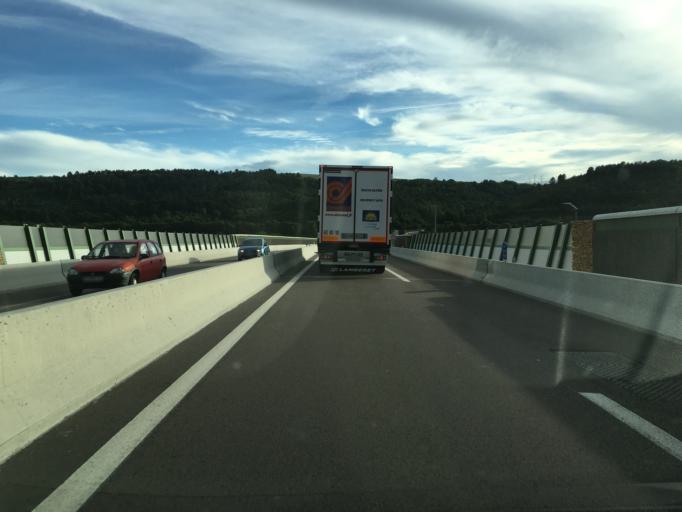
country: FR
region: Bourgogne
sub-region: Departement de la Cote-d'Or
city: Plombieres-les-Dijon
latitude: 47.3360
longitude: 4.9843
